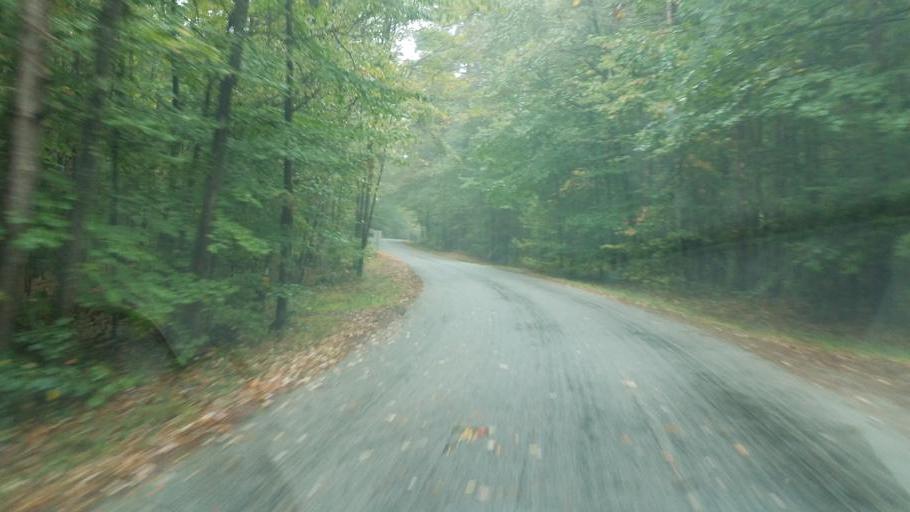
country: US
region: Ohio
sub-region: Ashland County
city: Loudonville
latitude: 40.6074
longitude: -82.2857
